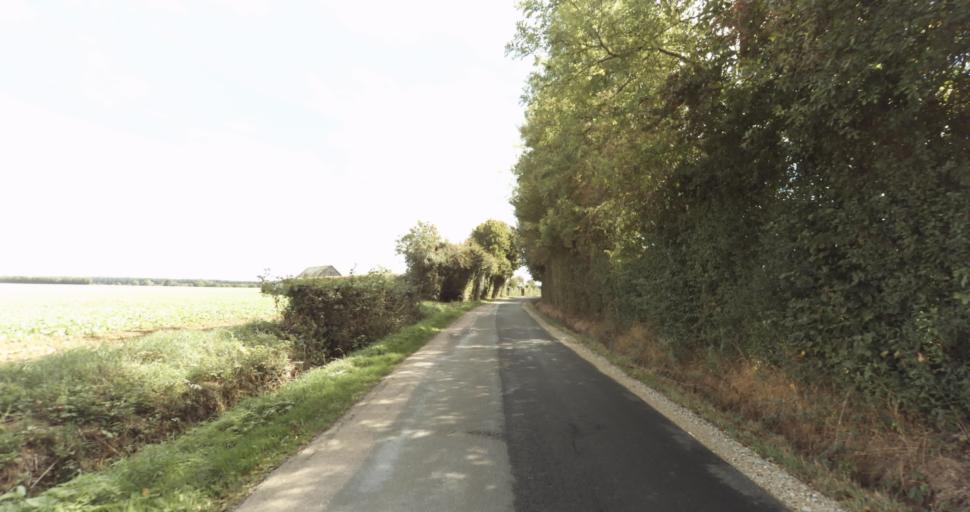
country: FR
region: Lower Normandy
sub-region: Departement de l'Orne
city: Gace
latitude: 48.8896
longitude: 0.3485
